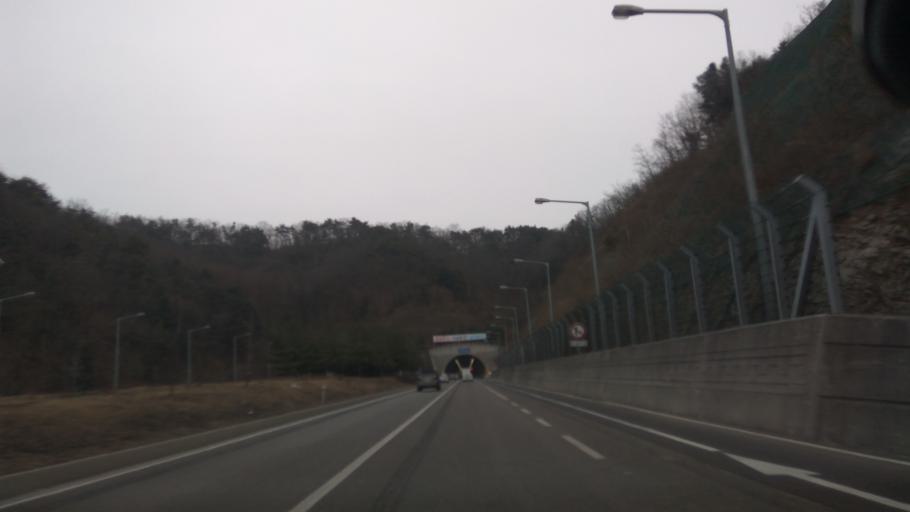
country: KR
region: Gangwon-do
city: Sindong
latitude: 37.7403
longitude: 127.6568
